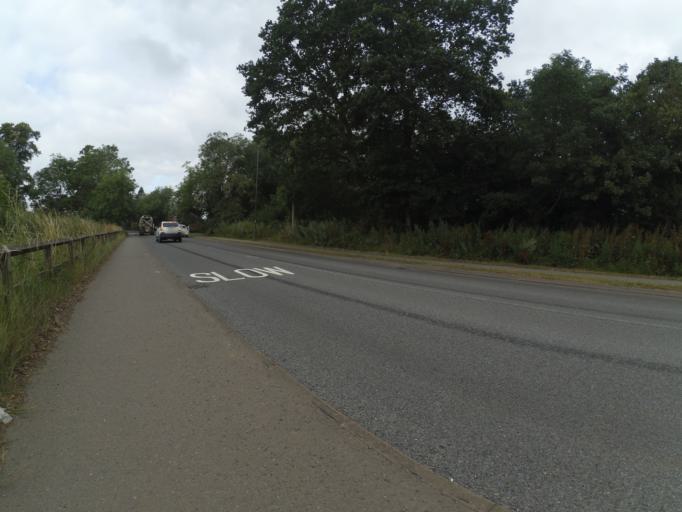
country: GB
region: England
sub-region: Warwickshire
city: Dunchurch
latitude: 52.3447
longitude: -1.2820
